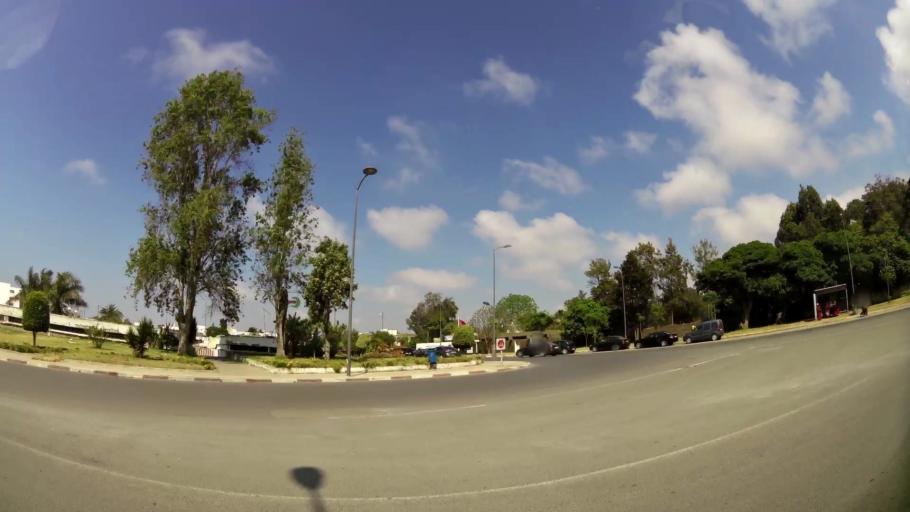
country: MA
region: Rabat-Sale-Zemmour-Zaer
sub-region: Rabat
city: Rabat
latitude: 33.9812
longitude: -6.8650
